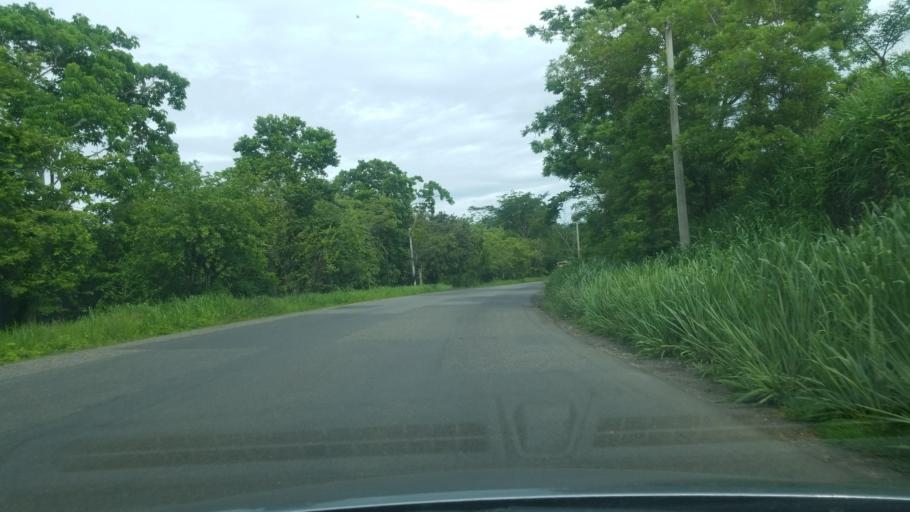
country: HN
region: Santa Barbara
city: Camalote
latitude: 15.3272
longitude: -88.3265
